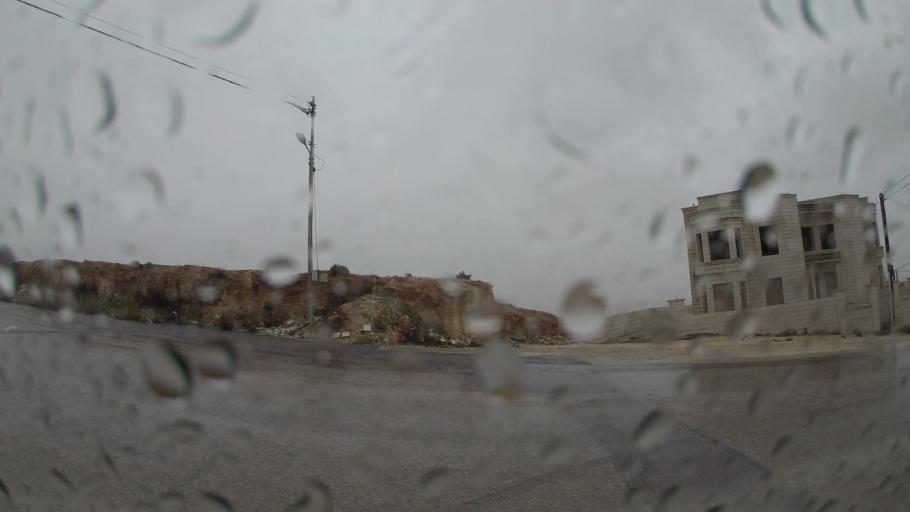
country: JO
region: Amman
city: Al Jubayhah
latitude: 32.0120
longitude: 35.8981
